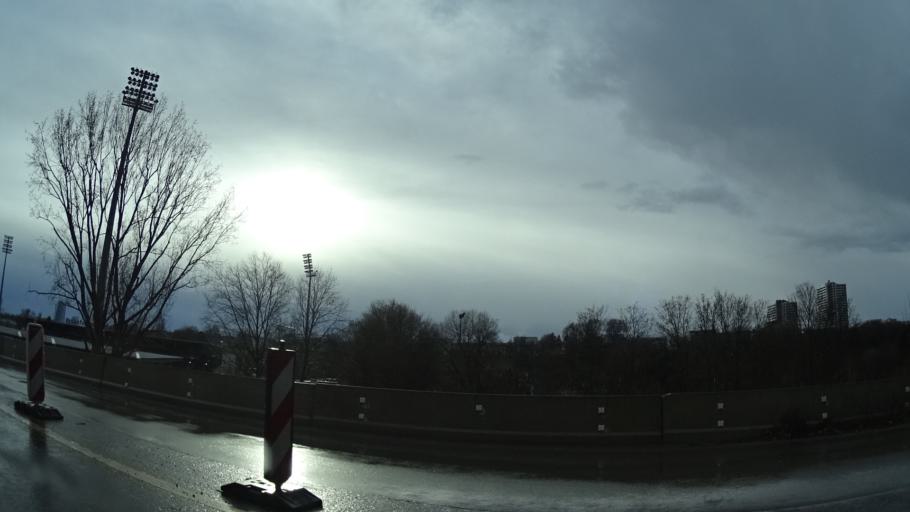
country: DE
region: Hesse
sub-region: Regierungsbezirk Darmstadt
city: Frankfurt am Main
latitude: 50.1294
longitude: 8.7243
